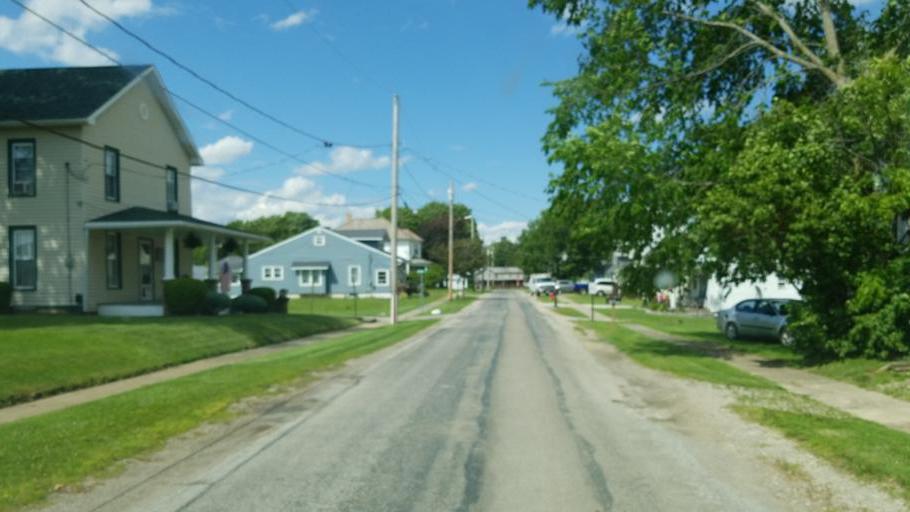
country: US
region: Ohio
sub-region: Huron County
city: Plymouth
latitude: 40.9651
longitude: -82.6002
